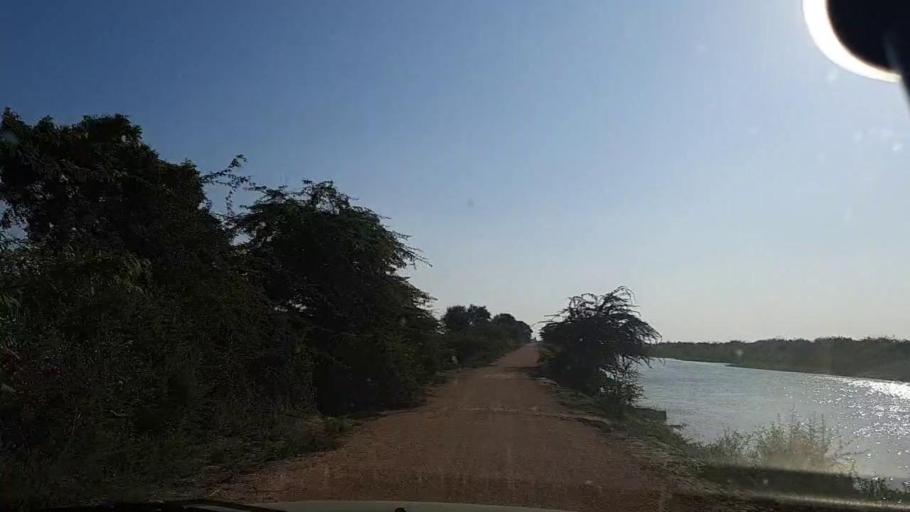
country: PK
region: Sindh
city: Chuhar Jamali
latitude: 24.5561
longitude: 68.0376
